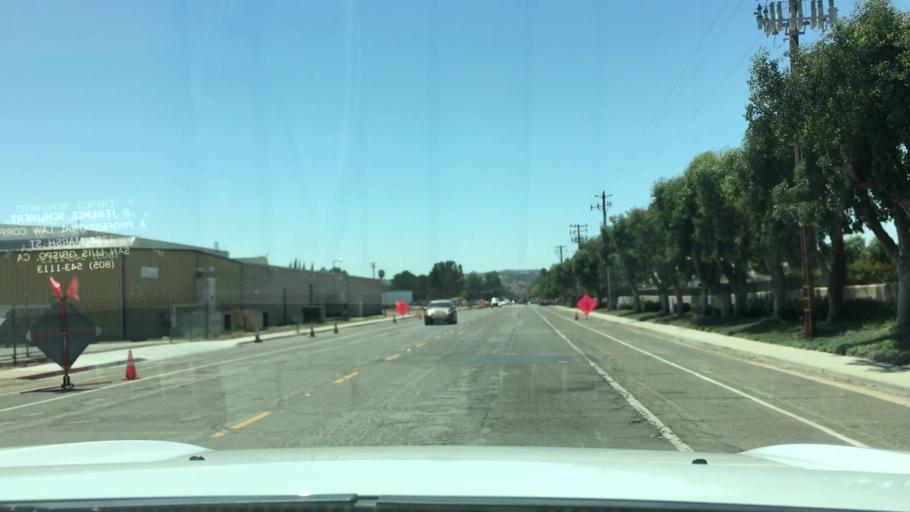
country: US
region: California
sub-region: San Luis Obispo County
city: Paso Robles
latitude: 35.6157
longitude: -120.6546
